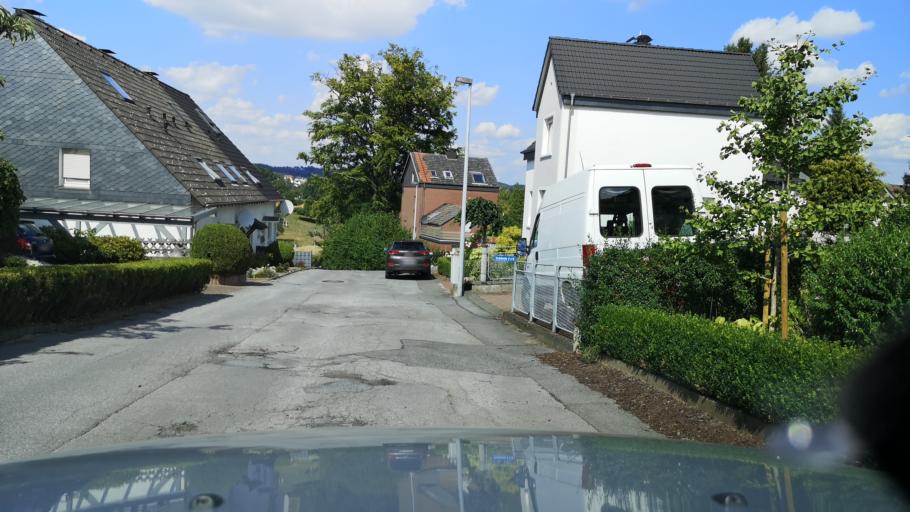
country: DE
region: North Rhine-Westphalia
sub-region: Regierungsbezirk Arnsberg
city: Frondenberg
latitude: 51.4582
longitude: 7.7662
